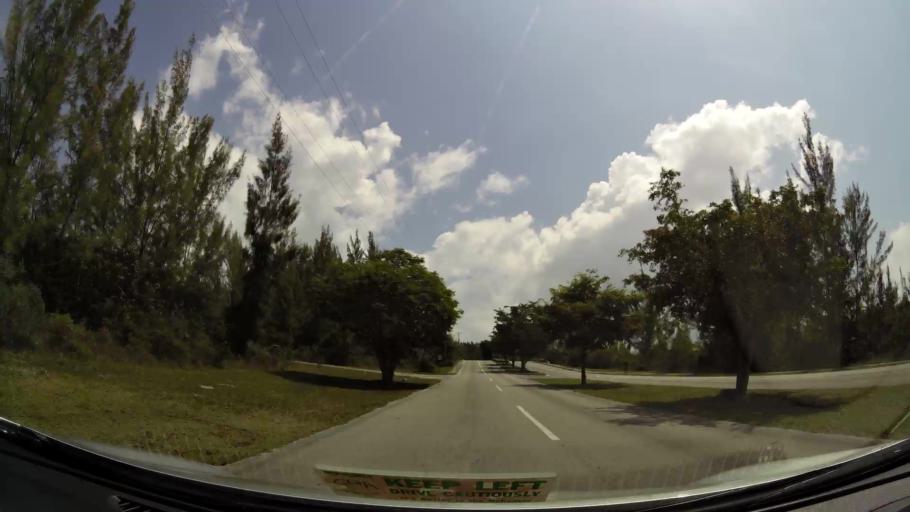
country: BS
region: Freeport
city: Lucaya
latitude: 26.5211
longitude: -78.6271
